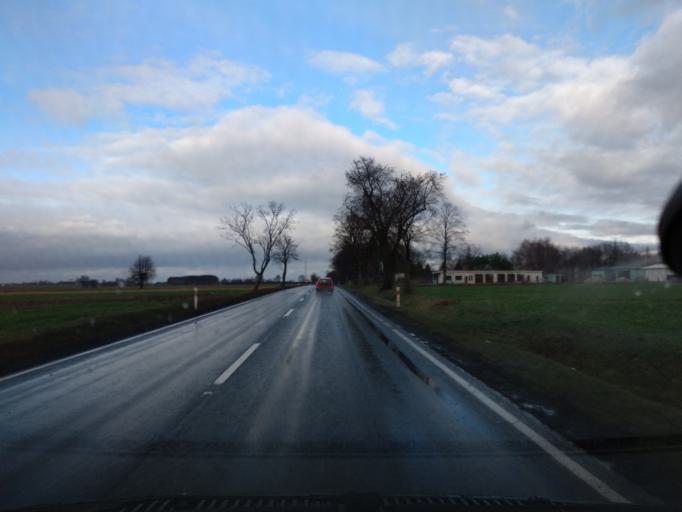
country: PL
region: Greater Poland Voivodeship
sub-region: Powiat koninski
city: Rychwal
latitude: 52.0435
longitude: 18.1621
